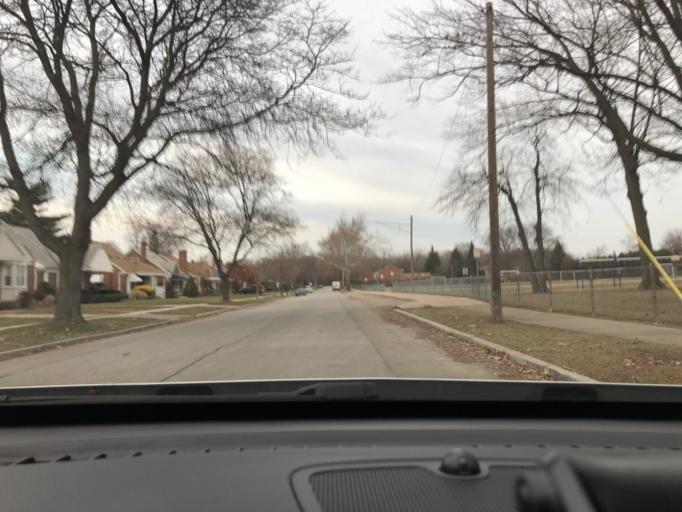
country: US
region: Michigan
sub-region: Wayne County
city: Allen Park
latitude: 42.2875
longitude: -83.2258
